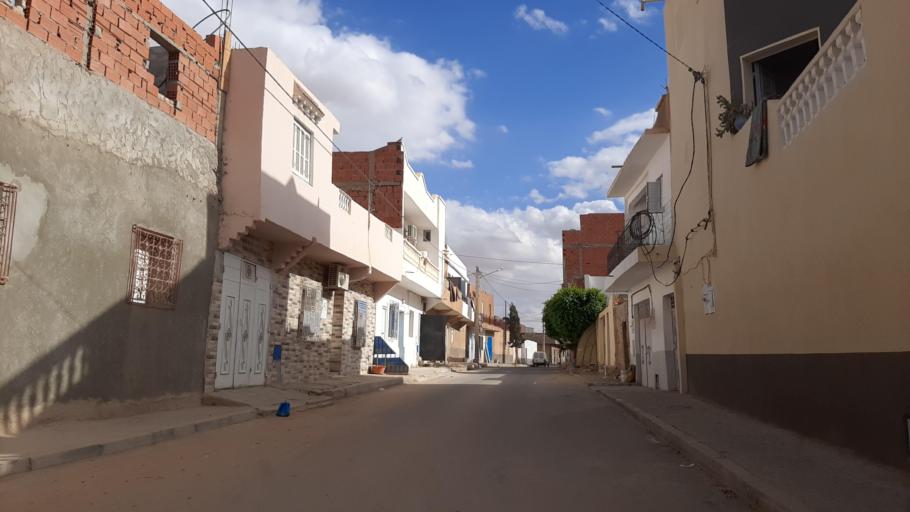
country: TN
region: Tataouine
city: Tataouine
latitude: 32.9307
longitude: 10.4544
